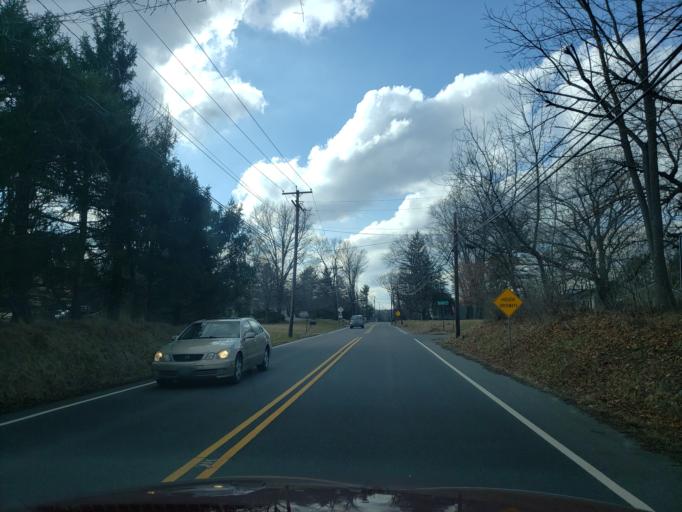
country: US
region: New Jersey
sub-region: Hunterdon County
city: Flemington
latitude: 40.4988
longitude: -74.8773
